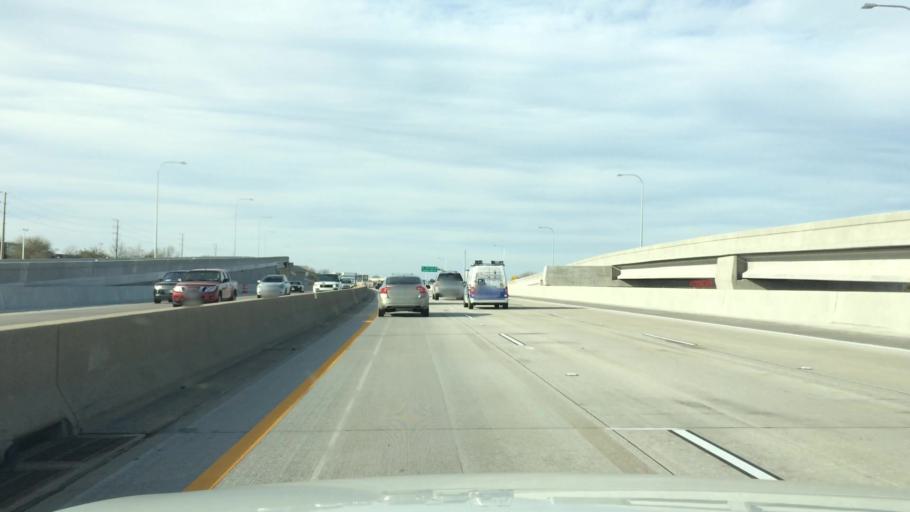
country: US
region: Texas
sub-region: Dallas County
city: Addison
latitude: 33.0193
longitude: -96.8290
